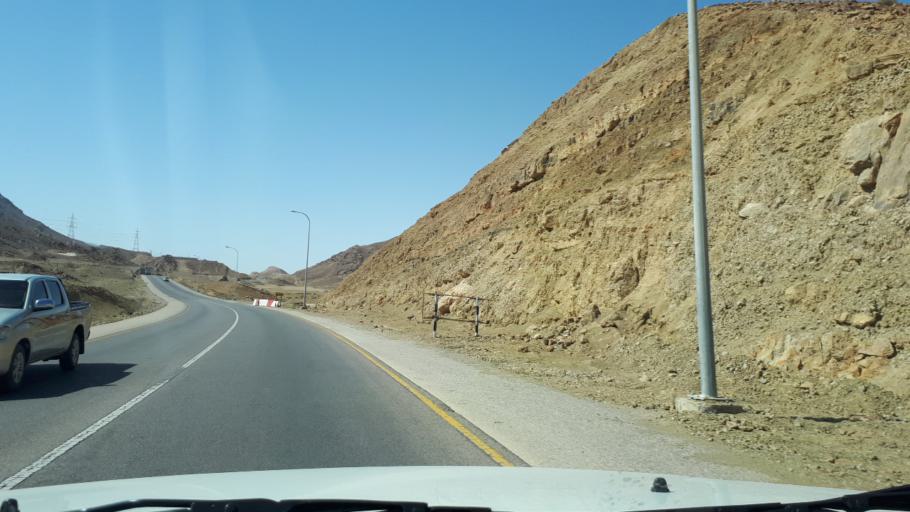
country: OM
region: Ash Sharqiyah
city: Sur
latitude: 22.3332
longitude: 59.3070
